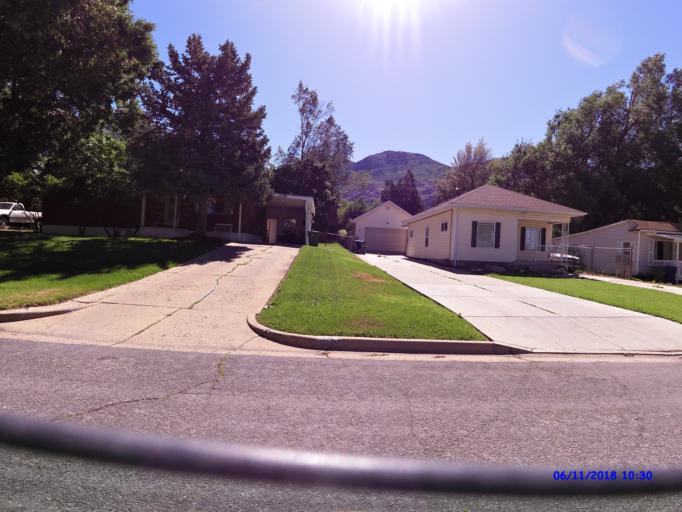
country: US
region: Utah
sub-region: Weber County
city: Ogden
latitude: 41.2294
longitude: -111.9423
